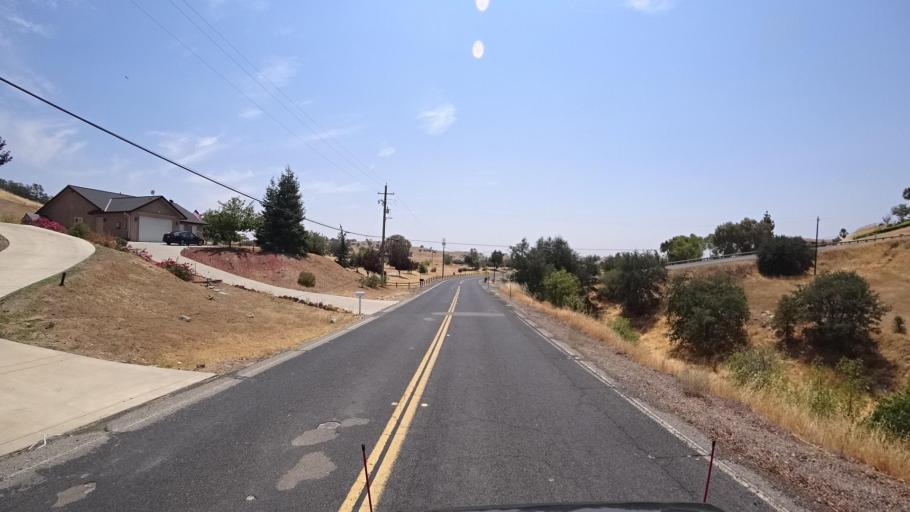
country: US
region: California
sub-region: Tuolumne County
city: Jamestown
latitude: 37.6357
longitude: -120.3508
